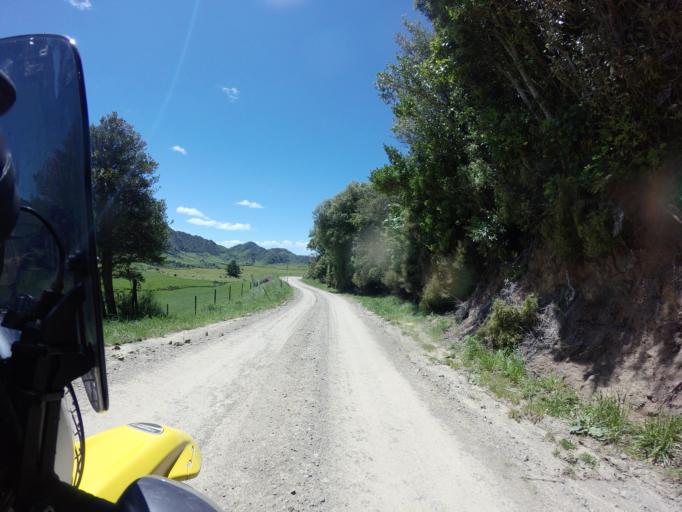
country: NZ
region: Bay of Plenty
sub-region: Opotiki District
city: Opotiki
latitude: -38.4051
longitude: 177.4492
